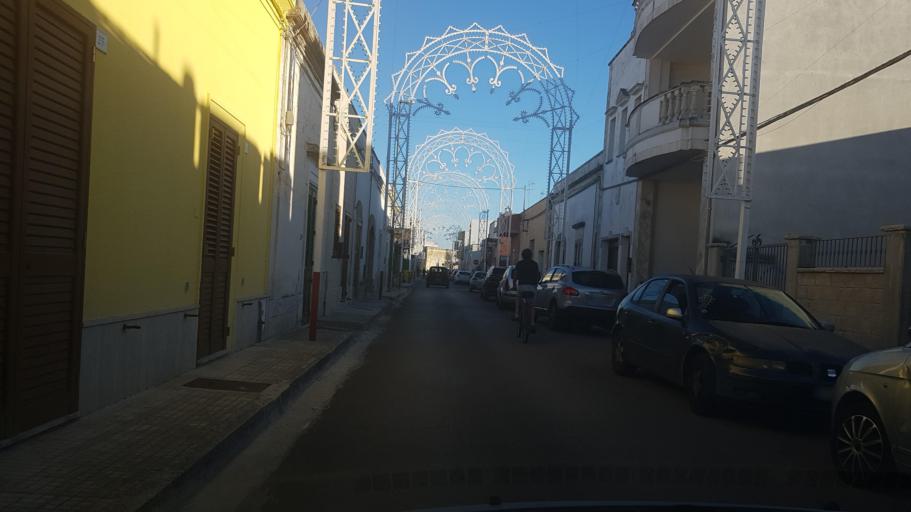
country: IT
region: Apulia
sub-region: Provincia di Lecce
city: Struda
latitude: 40.3199
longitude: 18.2822
